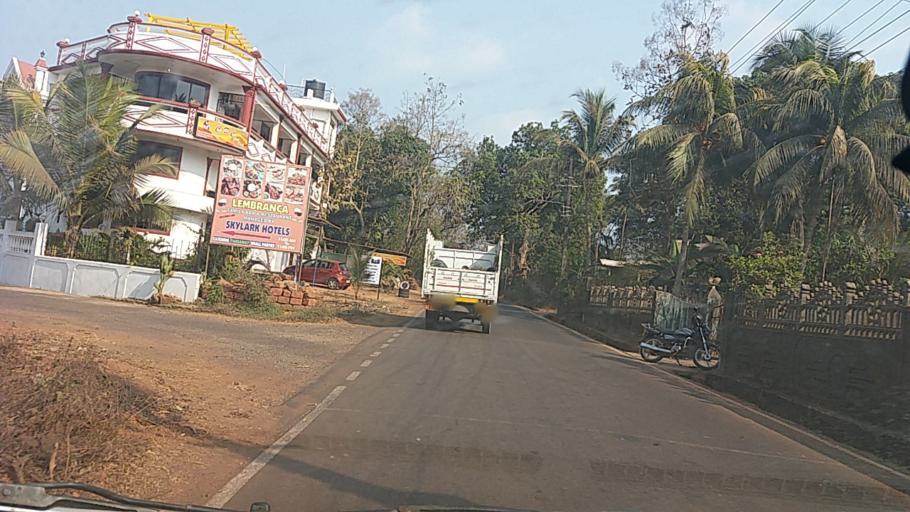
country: IN
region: Goa
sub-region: North Goa
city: Goa Velha
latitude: 15.4796
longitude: 73.9235
